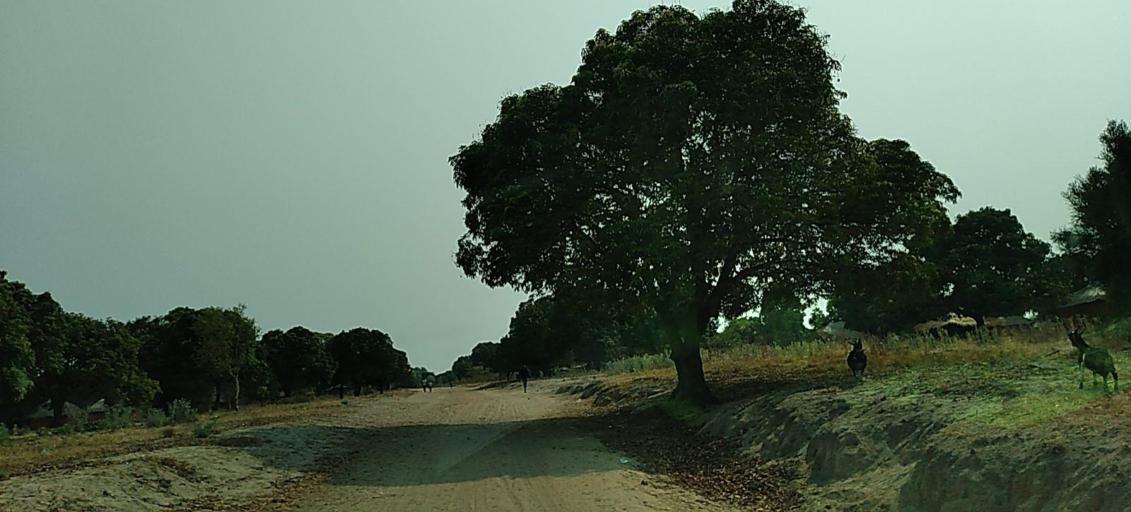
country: ZM
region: North-Western
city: Zambezi
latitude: -13.1721
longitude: 23.4034
